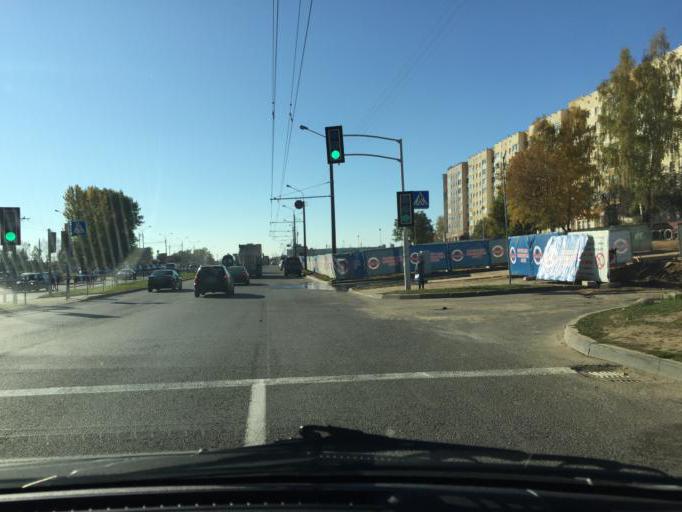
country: BY
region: Minsk
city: Syenitsa
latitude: 53.8462
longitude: 27.5351
